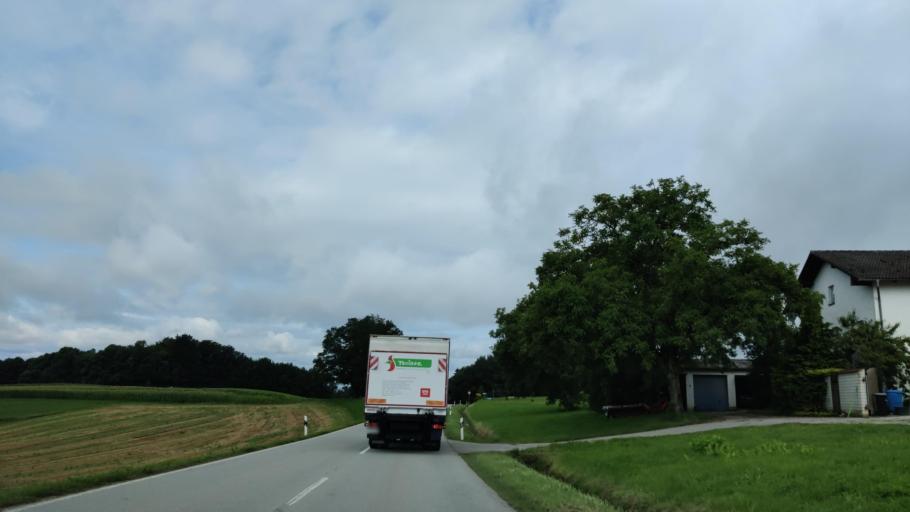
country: DE
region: Bavaria
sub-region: Lower Bavaria
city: Hofkirchen
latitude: 48.6798
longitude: 13.1483
